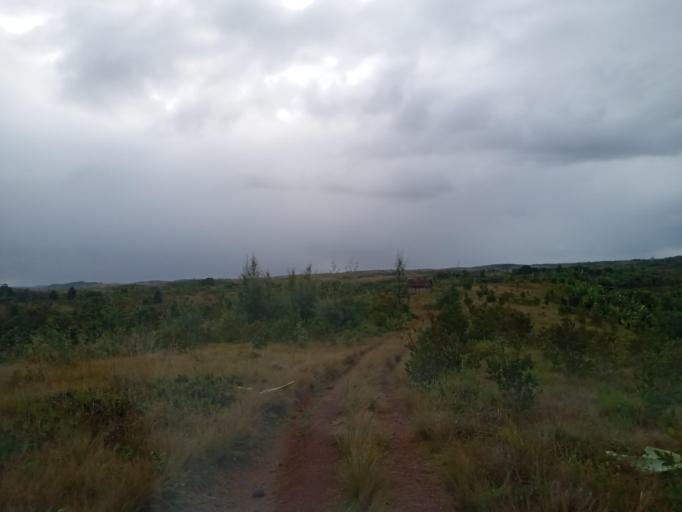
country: MG
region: Atsimo-Atsinanana
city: Vohipaho
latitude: -24.0005
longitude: 47.4045
